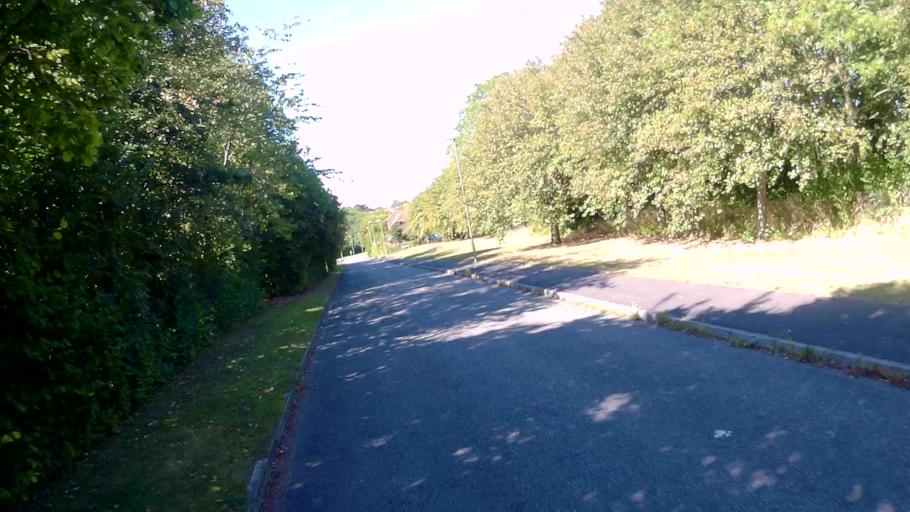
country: GB
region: England
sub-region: Hampshire
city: Basingstoke
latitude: 51.2398
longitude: -1.1283
